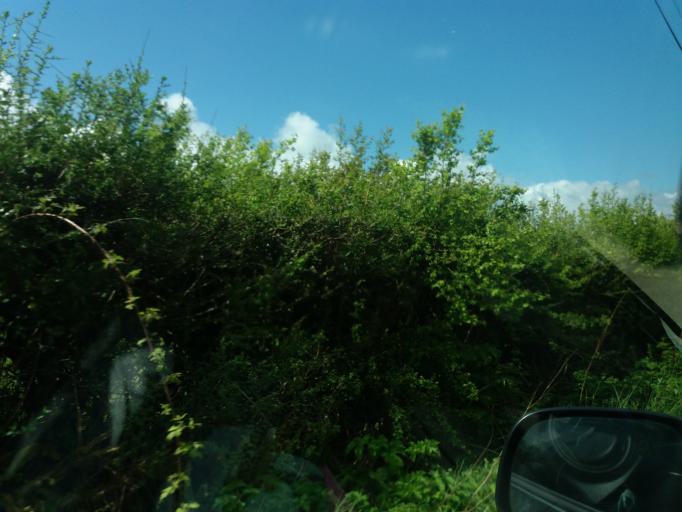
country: IE
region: Munster
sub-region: Waterford
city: Dunmore East
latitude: 52.2152
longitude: -6.9075
